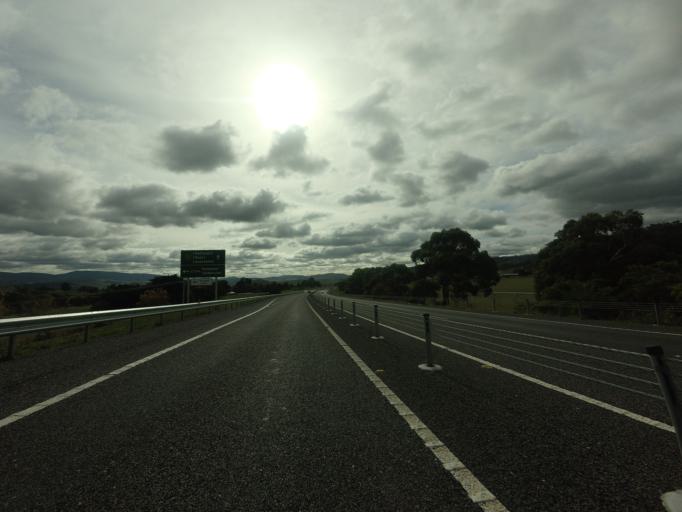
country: AU
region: Tasmania
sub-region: Brighton
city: Bridgewater
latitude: -42.5438
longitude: 147.2067
